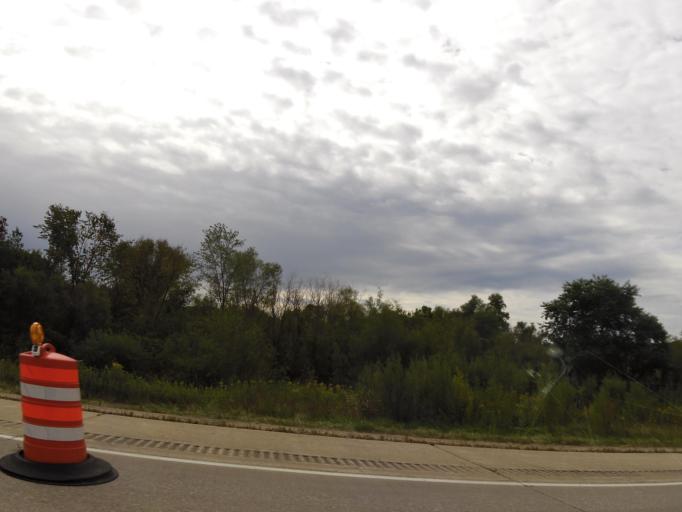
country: US
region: Wisconsin
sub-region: Monroe County
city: Sparta
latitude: 43.9057
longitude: -90.8914
